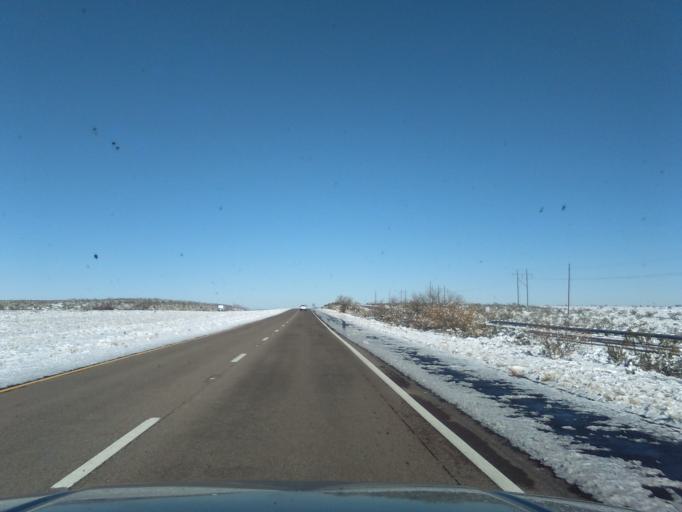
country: US
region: New Mexico
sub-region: Socorro County
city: Socorro
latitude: 33.6492
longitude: -107.1064
